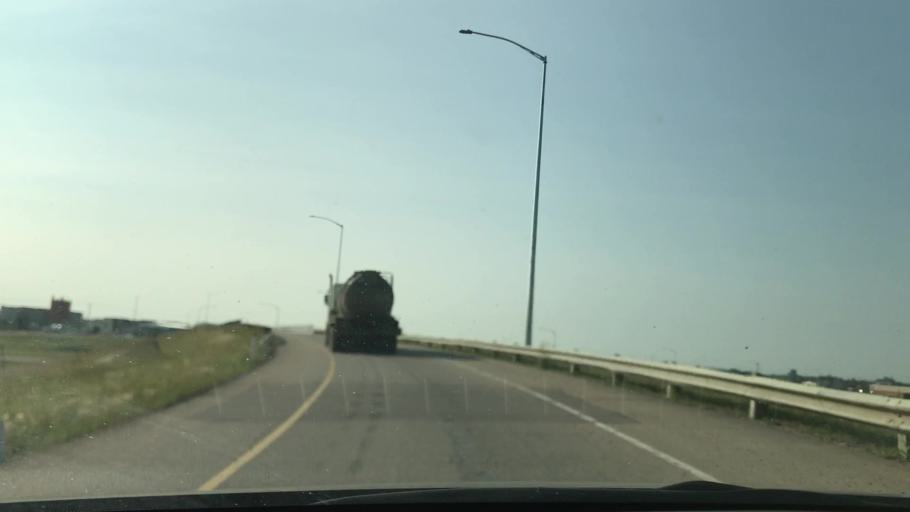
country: CA
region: Alberta
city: Leduc
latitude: 53.2854
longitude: -113.5512
